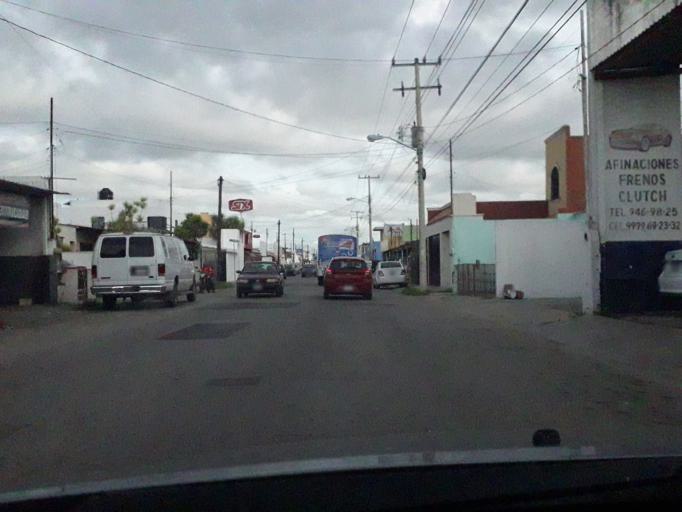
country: MX
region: Yucatan
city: Merida
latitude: 21.0214
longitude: -89.6420
